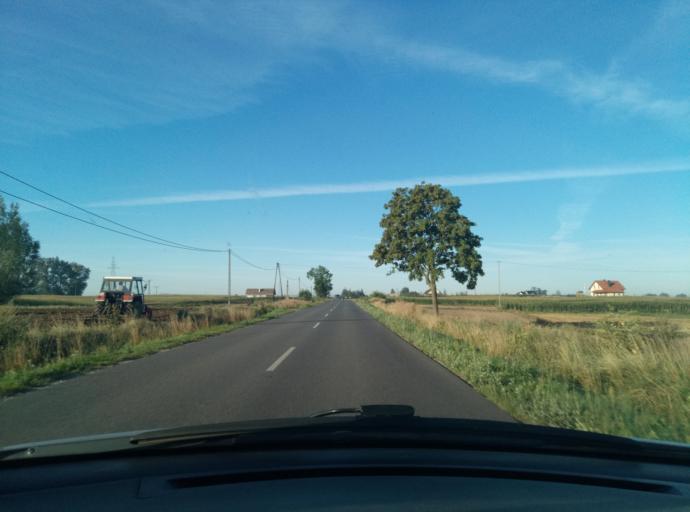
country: PL
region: Kujawsko-Pomorskie
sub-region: Powiat golubsko-dobrzynski
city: Kowalewo Pomorskie
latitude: 53.1864
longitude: 18.9076
